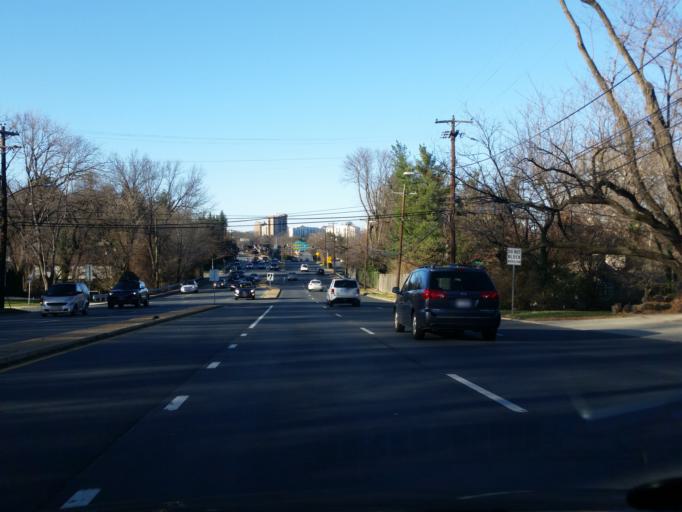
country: US
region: Maryland
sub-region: Montgomery County
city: South Kensington
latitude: 39.0115
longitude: -77.0978
